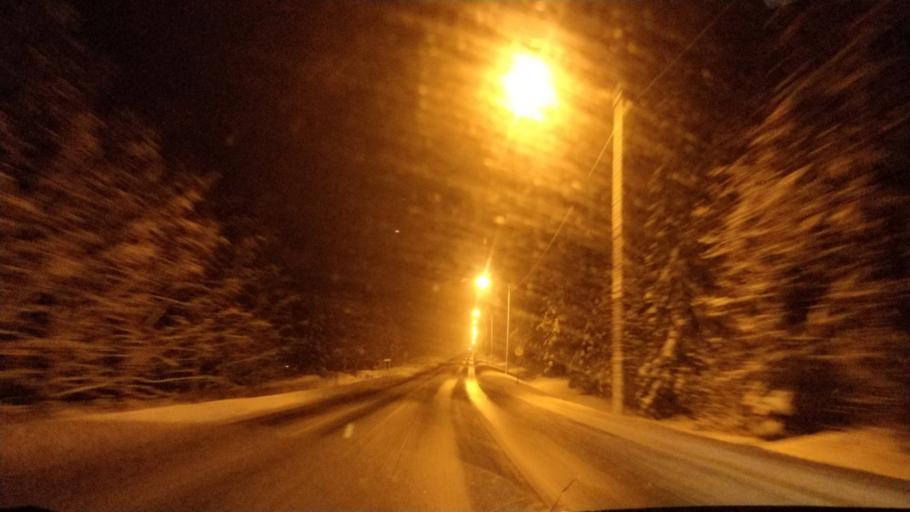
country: FI
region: Lapland
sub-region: Rovaniemi
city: Rovaniemi
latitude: 66.4145
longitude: 25.4107
